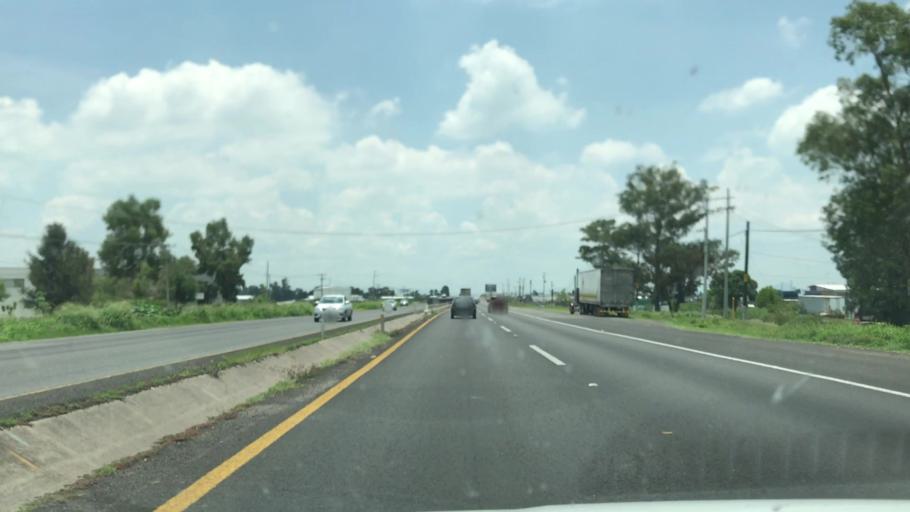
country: MX
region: Guanajuato
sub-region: Irapuato
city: San Jose de Bernalejo (El Guayabo)
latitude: 20.6092
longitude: -101.4097
